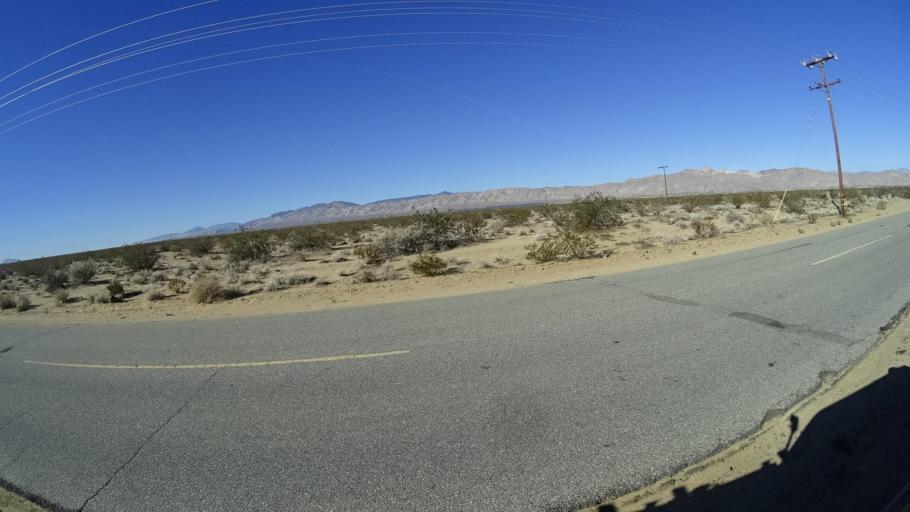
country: US
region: California
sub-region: Kern County
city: California City
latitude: 35.1835
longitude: -117.9849
